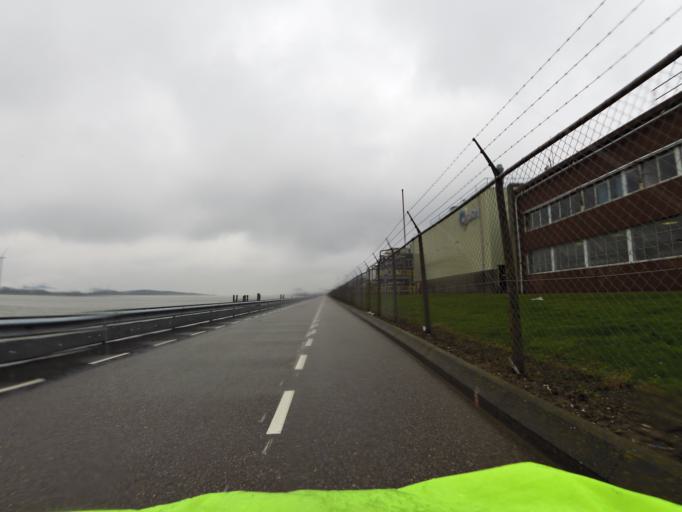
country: NL
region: South Holland
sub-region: Gemeente Rotterdam
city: Hoek van Holland
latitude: 51.9639
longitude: 4.1530
